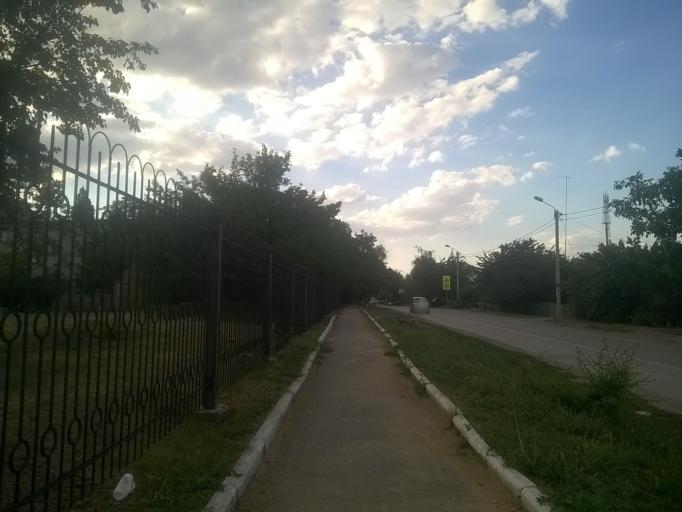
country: RU
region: Rostov
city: Donetsk
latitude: 48.3332
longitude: 39.9522
